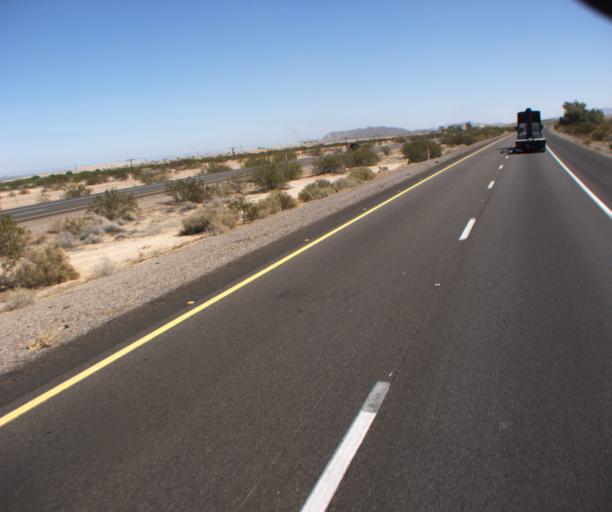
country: US
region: Arizona
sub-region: Yuma County
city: Wellton
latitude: 32.6719
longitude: -114.0983
